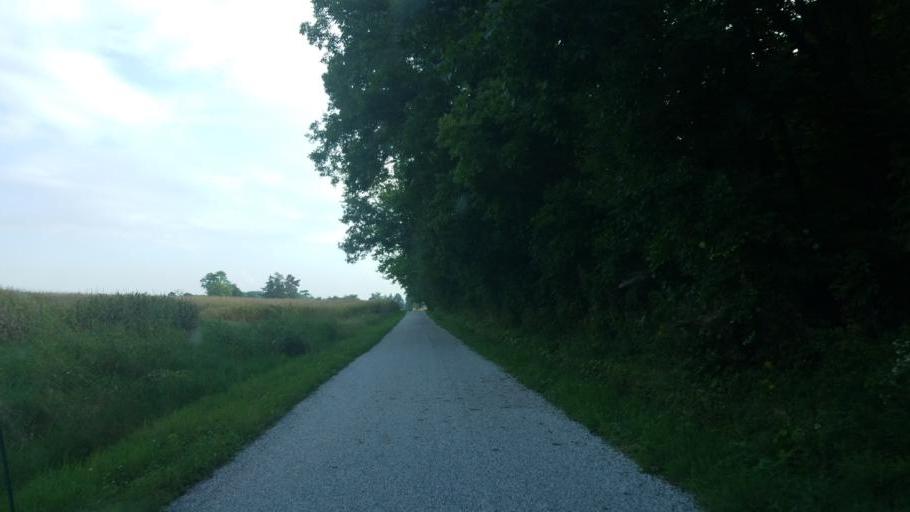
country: US
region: Ohio
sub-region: Wayne County
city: Wooster
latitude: 40.8053
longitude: -82.0421
